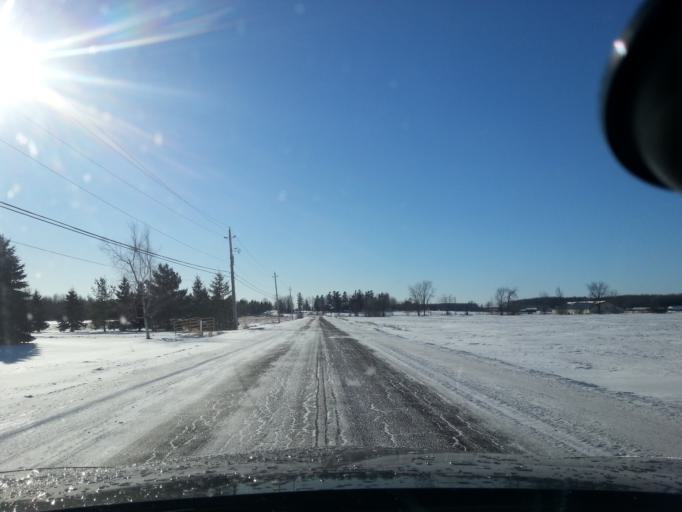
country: CA
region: Ontario
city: Clarence-Rockland
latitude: 45.3041
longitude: -75.3892
